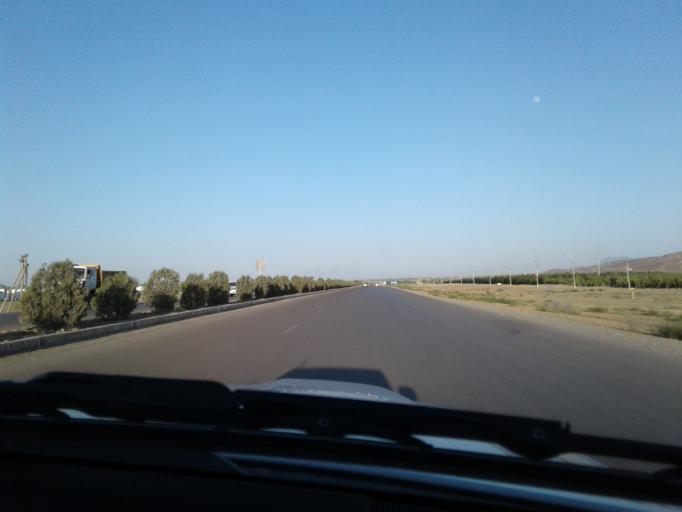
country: TM
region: Ahal
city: Baharly
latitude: 38.2747
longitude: 57.6903
